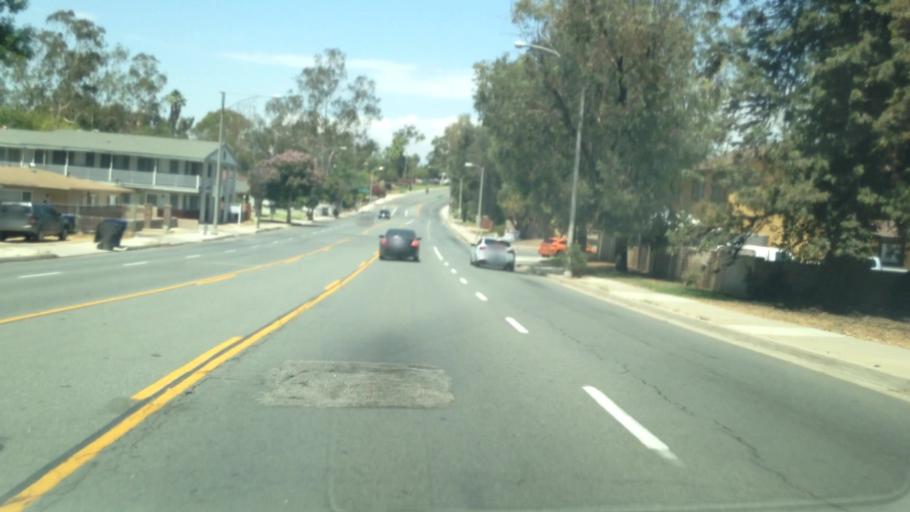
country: US
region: California
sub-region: Riverside County
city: Riverside
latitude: 33.9661
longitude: -117.3795
